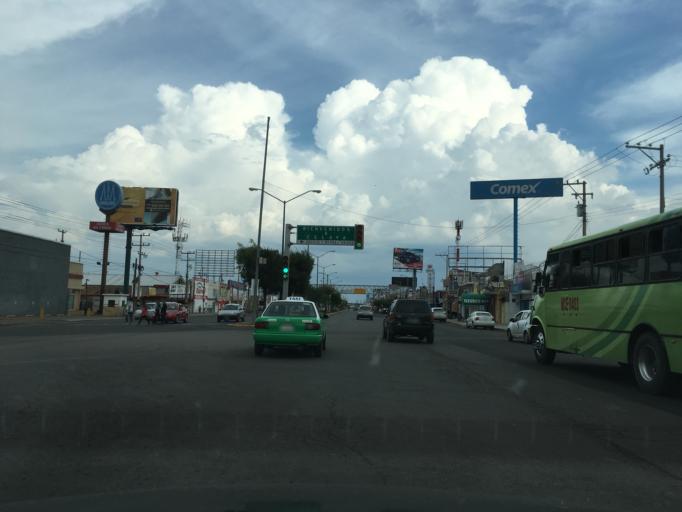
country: MX
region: Guanajuato
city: Celaya
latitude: 20.5443
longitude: -100.8212
